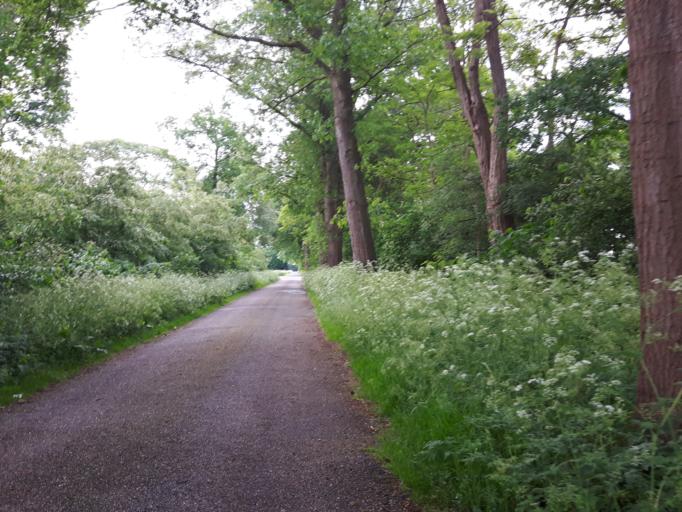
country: NL
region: Overijssel
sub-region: Gemeente Enschede
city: Enschede
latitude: 52.1710
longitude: 6.8516
